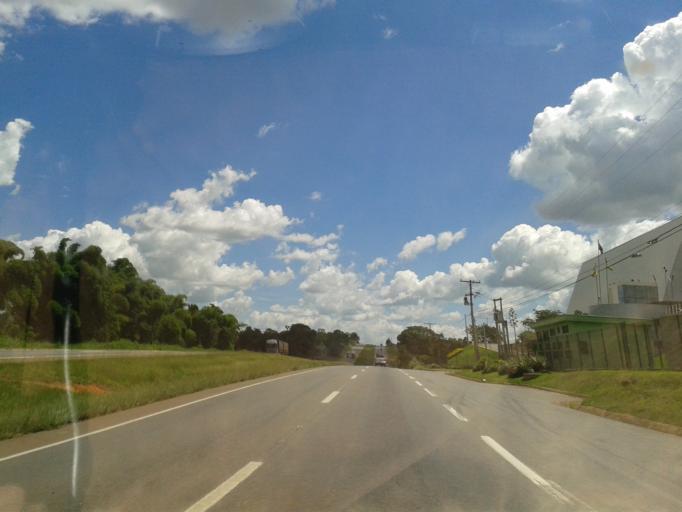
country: BR
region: Goias
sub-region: Aparecida De Goiania
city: Aparecida de Goiania
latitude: -16.8559
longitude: -49.2483
